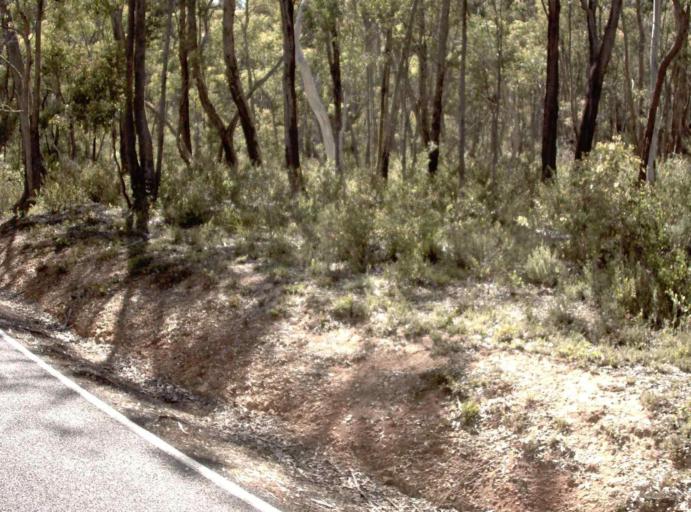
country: AU
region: New South Wales
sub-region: Bombala
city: Bombala
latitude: -37.1380
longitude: 148.7348
